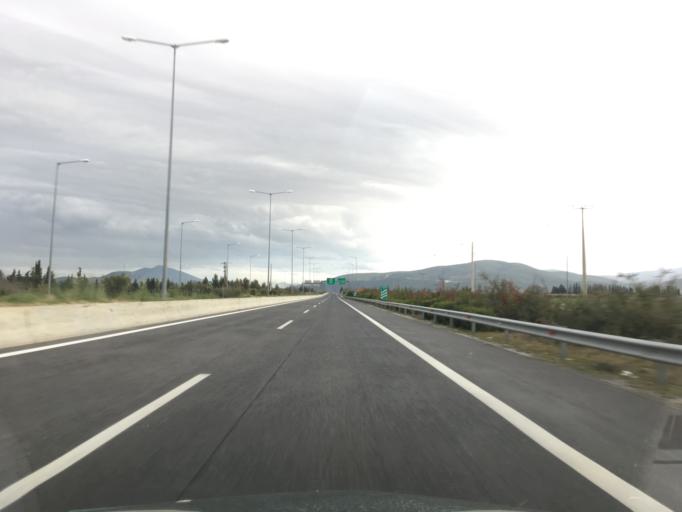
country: GR
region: Thessaly
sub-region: Nomos Magnisias
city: Almyros
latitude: 39.1982
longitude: 22.7642
